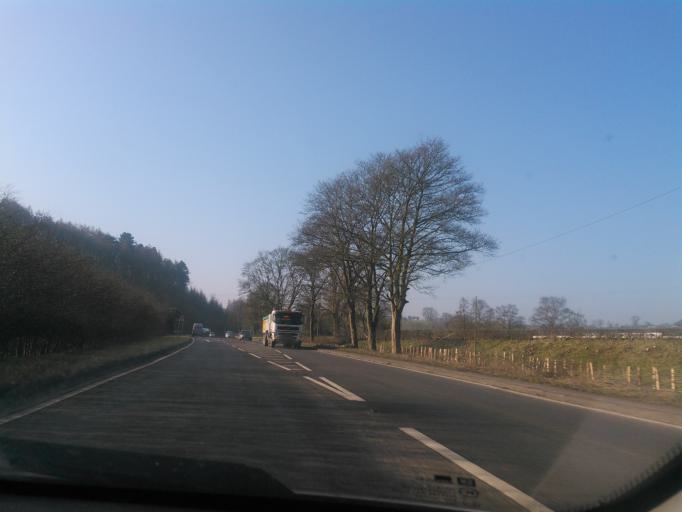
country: GB
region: England
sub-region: Shropshire
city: Church Stretton
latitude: 52.5168
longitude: -2.8216
